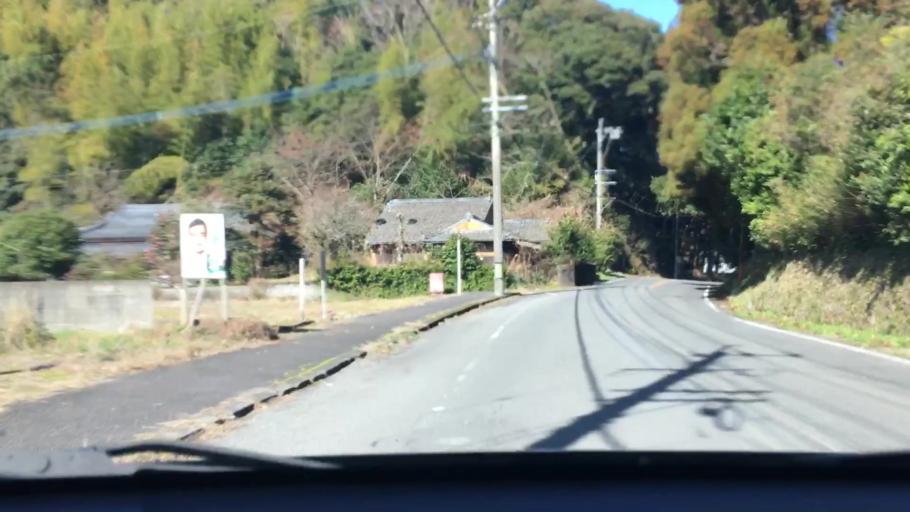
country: JP
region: Kagoshima
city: Satsumasendai
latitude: 31.7809
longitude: 130.3989
